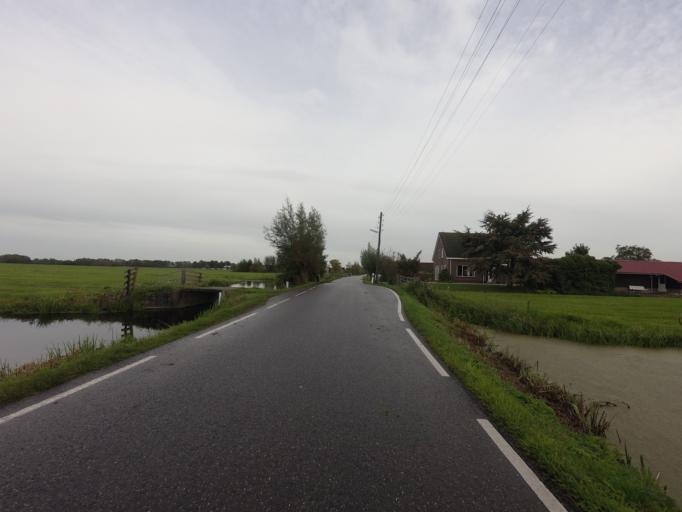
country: NL
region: South Holland
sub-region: Molenwaard
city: Liesveld
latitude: 51.9368
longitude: 4.7695
